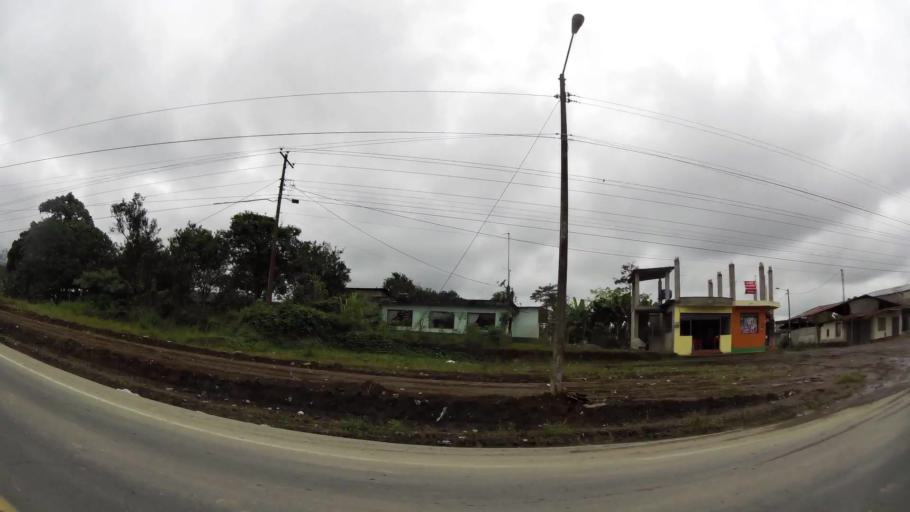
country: EC
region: Santo Domingo de los Tsachilas
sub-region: Canton Santo Domingo de los Colorados
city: Santo Domingo de los Colorados
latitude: -0.2773
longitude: -79.1721
